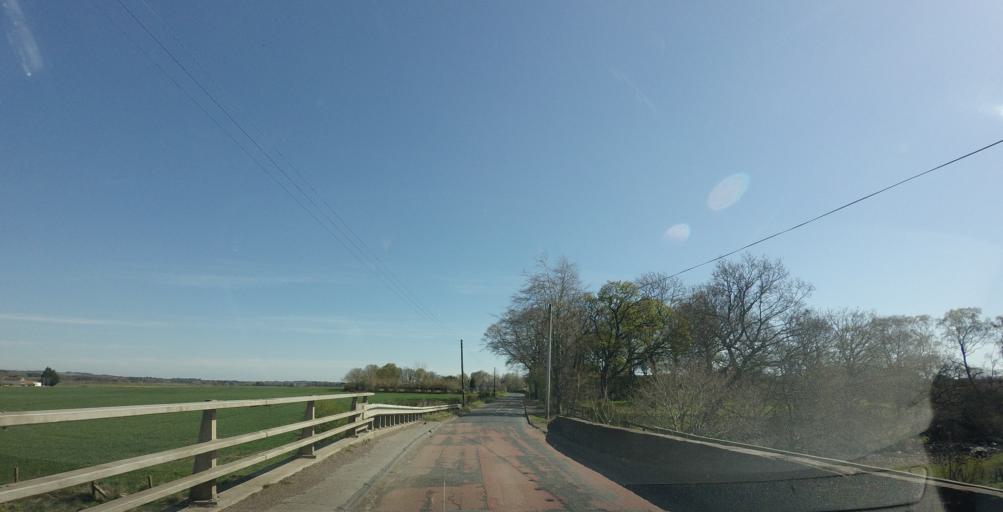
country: GB
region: Scotland
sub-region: West Lothian
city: West Calder
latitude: 55.8685
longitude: -3.5728
